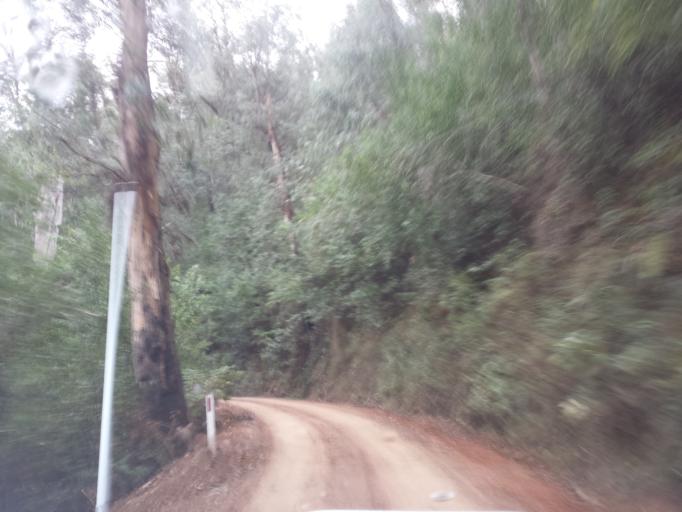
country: AU
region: Victoria
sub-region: Latrobe
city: Traralgon
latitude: -37.9960
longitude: 146.4678
